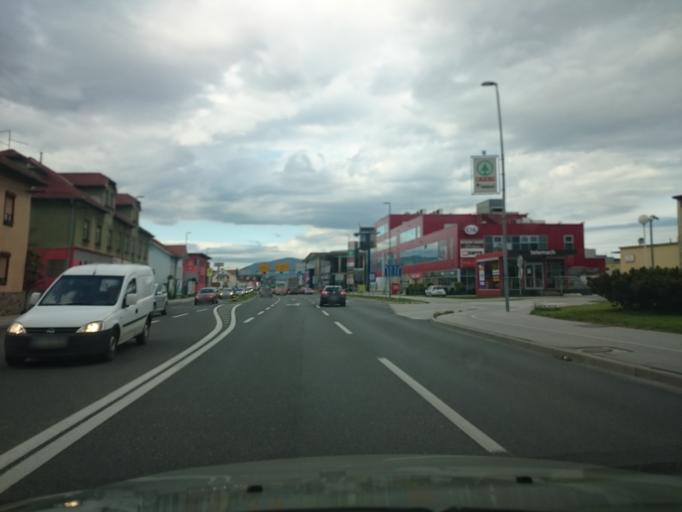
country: SI
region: Celje
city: Celje
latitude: 46.2395
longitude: 15.2743
